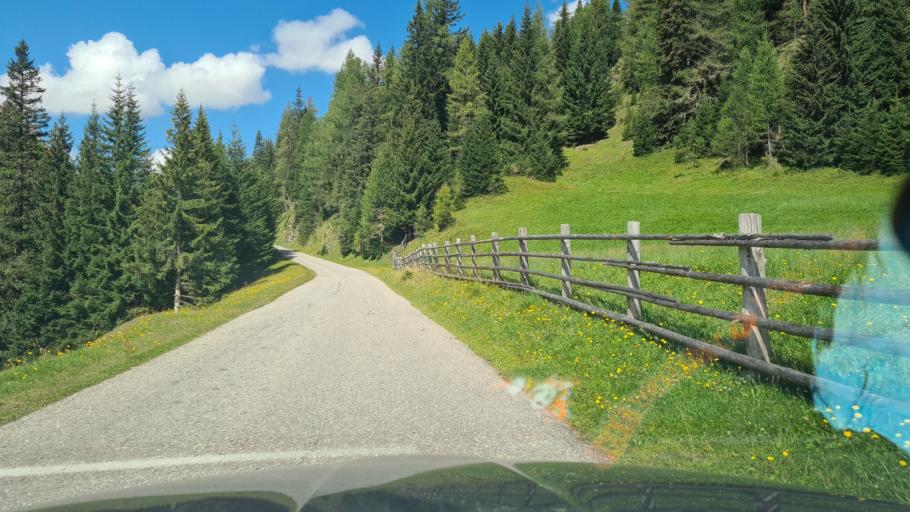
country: AT
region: Salzburg
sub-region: Politischer Bezirk Tamsweg
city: Zederhaus
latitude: 47.1861
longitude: 13.4188
